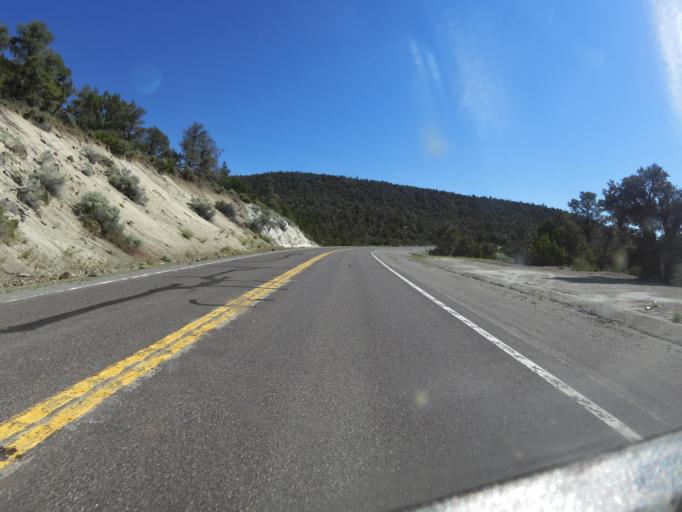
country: US
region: Nevada
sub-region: White Pine County
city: Ely
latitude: 38.8153
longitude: -115.2940
